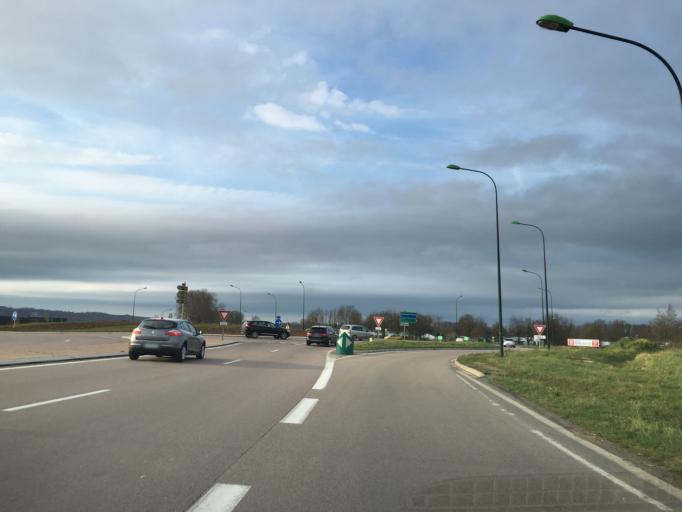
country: FR
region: Bourgogne
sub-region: Departement de l'Yonne
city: Maillot
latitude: 48.1736
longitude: 3.2943
